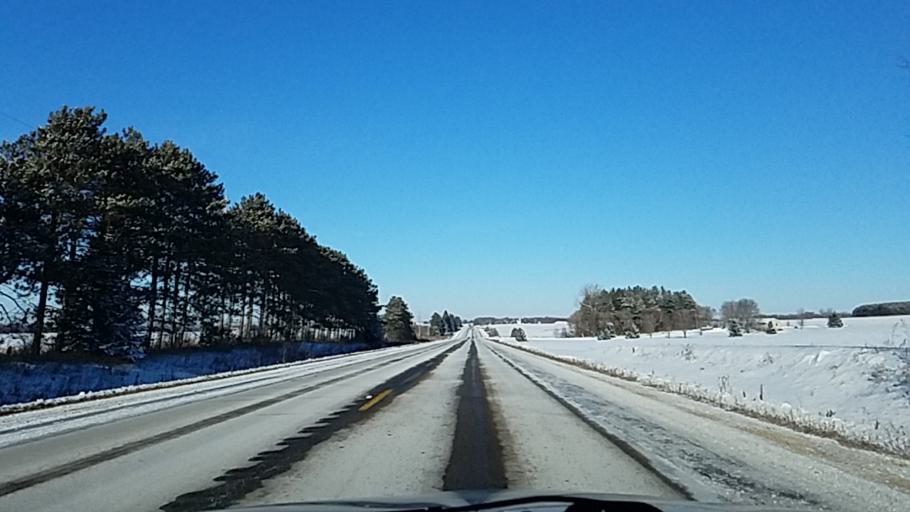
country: US
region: Wisconsin
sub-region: Saint Croix County
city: Roberts
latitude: 45.0397
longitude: -92.5374
